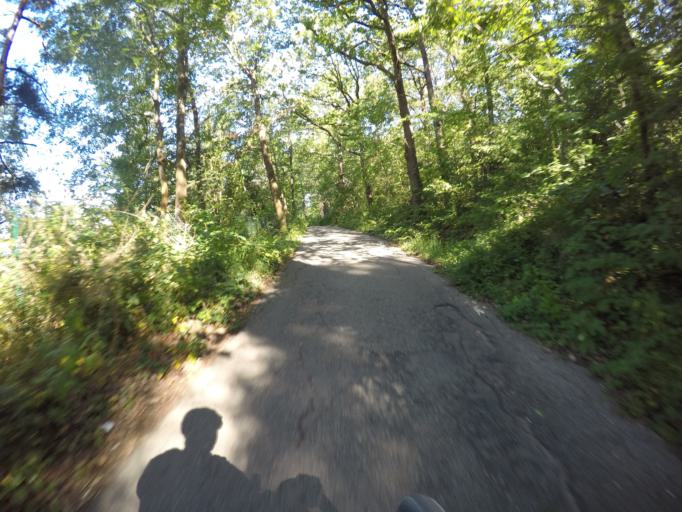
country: DE
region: Baden-Wuerttemberg
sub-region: Regierungsbezirk Stuttgart
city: Stuttgart-Ost
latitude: 48.7717
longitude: 9.2141
